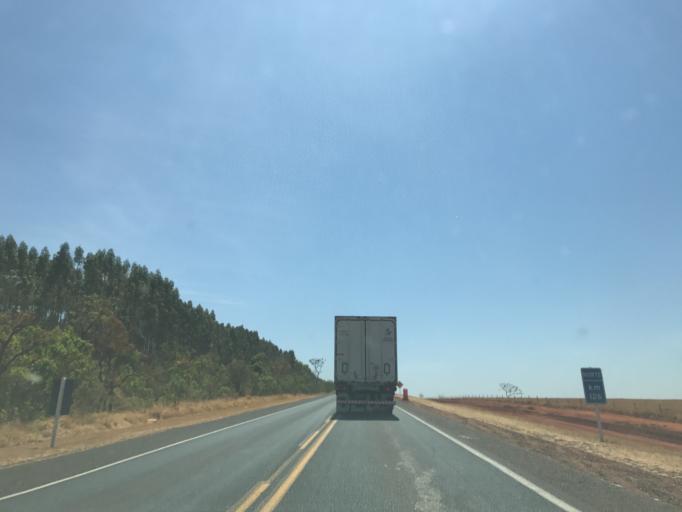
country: BR
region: Minas Gerais
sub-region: Prata
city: Prata
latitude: -19.4531
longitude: -48.8840
